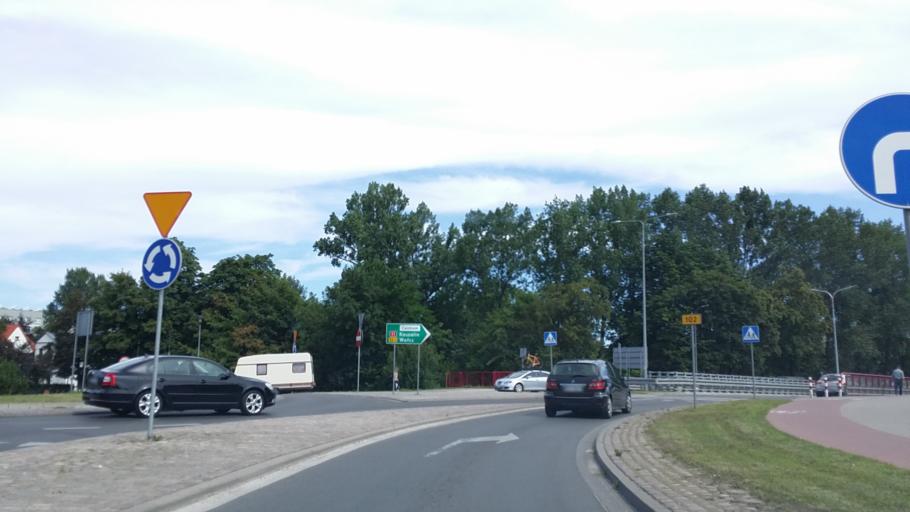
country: PL
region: West Pomeranian Voivodeship
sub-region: Powiat kolobrzeski
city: Kolobrzeg
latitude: 54.1716
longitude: 15.5713
